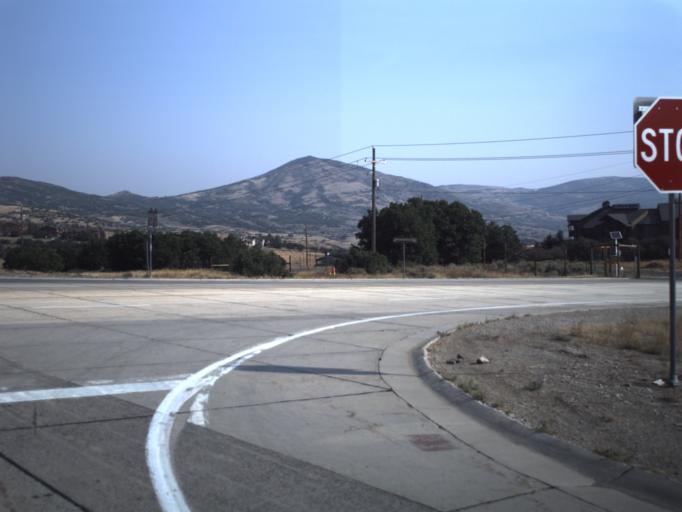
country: US
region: Utah
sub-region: Summit County
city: Park City
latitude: 40.6255
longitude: -111.4395
